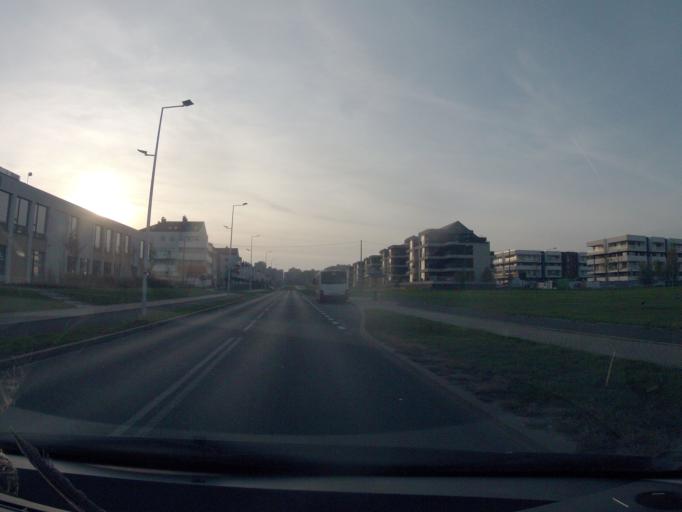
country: PL
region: Opole Voivodeship
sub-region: Powiat opolski
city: Opole
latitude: 50.6752
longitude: 17.9696
